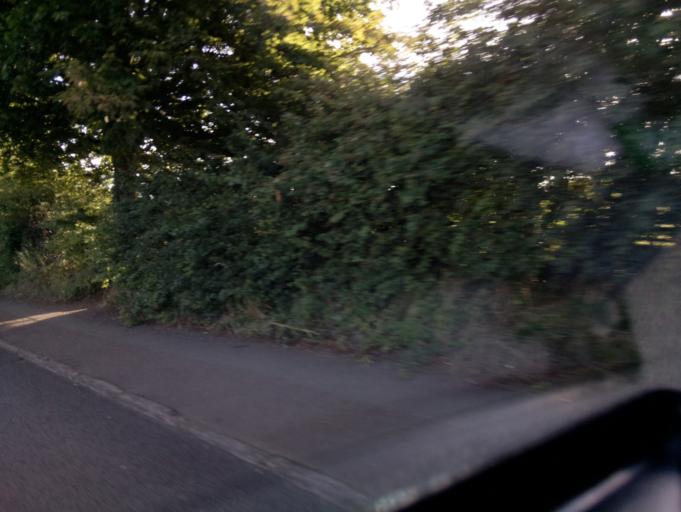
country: GB
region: England
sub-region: South Gloucestershire
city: Mangotsfield
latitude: 51.4925
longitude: -2.4857
